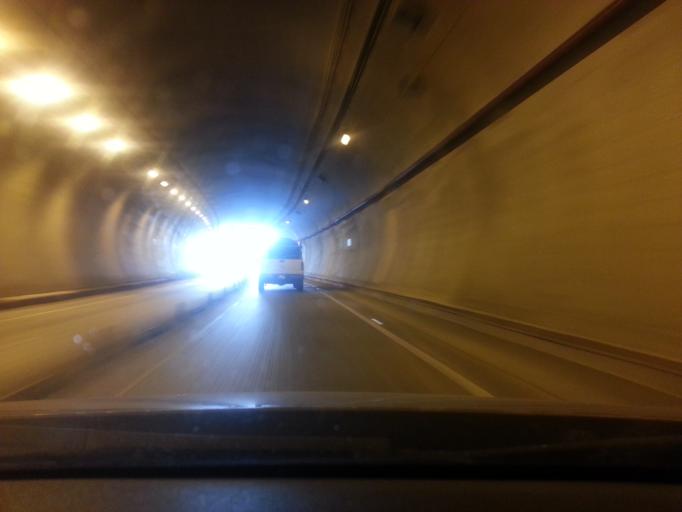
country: MX
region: Puebla
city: Xicotepec de Juarez
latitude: 20.2851
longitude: -97.9795
